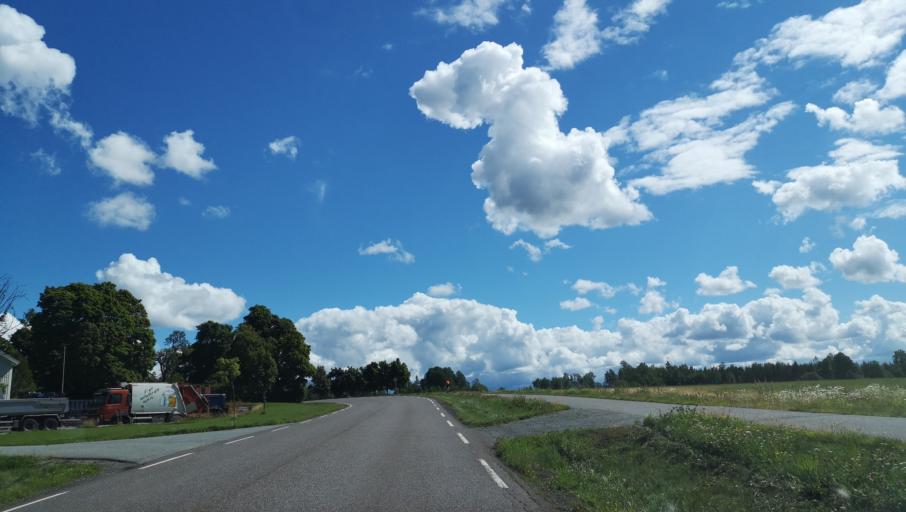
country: NO
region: Akershus
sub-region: Frogn
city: Drobak
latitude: 59.6570
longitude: 10.6911
